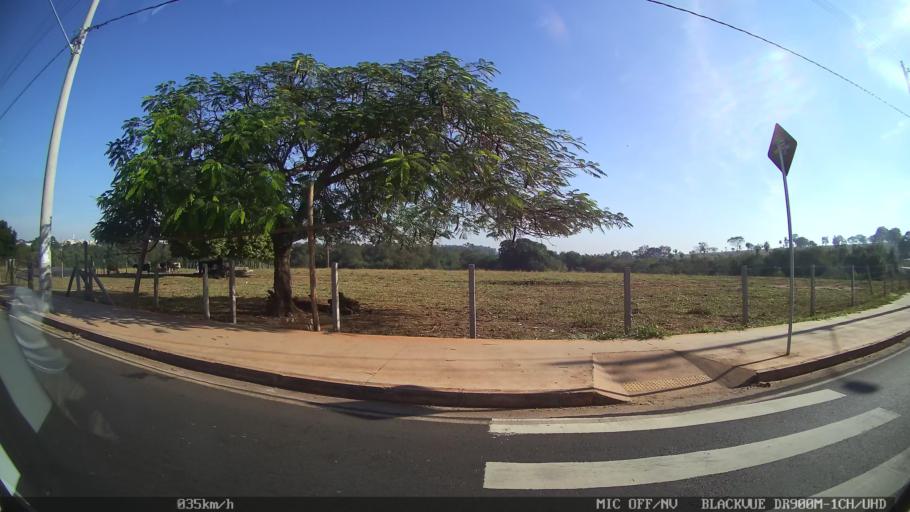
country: BR
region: Sao Paulo
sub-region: Sao Jose Do Rio Preto
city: Sao Jose do Rio Preto
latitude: -20.7602
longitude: -49.3717
